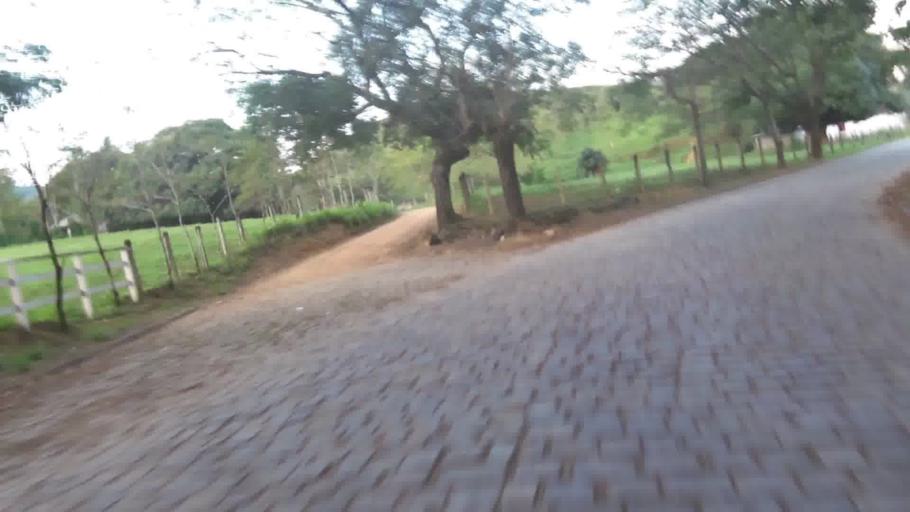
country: BR
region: Espirito Santo
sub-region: Alfredo Chaves
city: Alfredo Chaves
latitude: -20.6495
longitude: -40.6434
